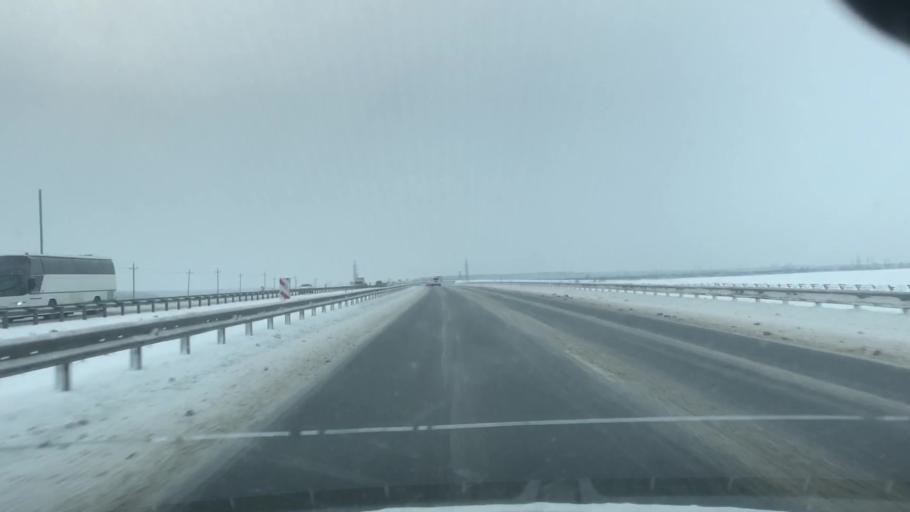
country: RU
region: Moskovskaya
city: Mikhnevo
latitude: 55.1059
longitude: 37.9264
